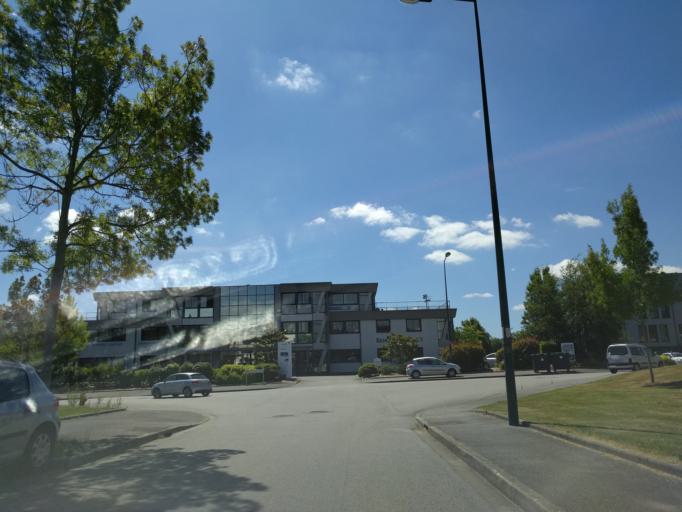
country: FR
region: Brittany
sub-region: Departement du Finistere
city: Quimper
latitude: 47.9779
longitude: -4.1042
